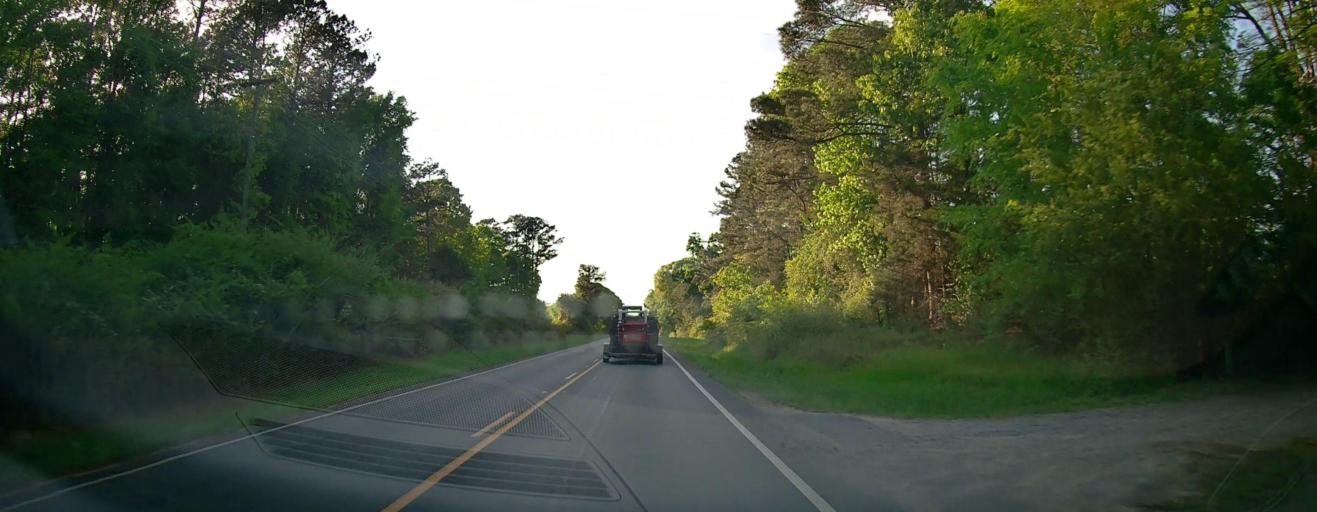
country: US
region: Georgia
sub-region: Putnam County
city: Eatonton
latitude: 33.3288
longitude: -83.5021
